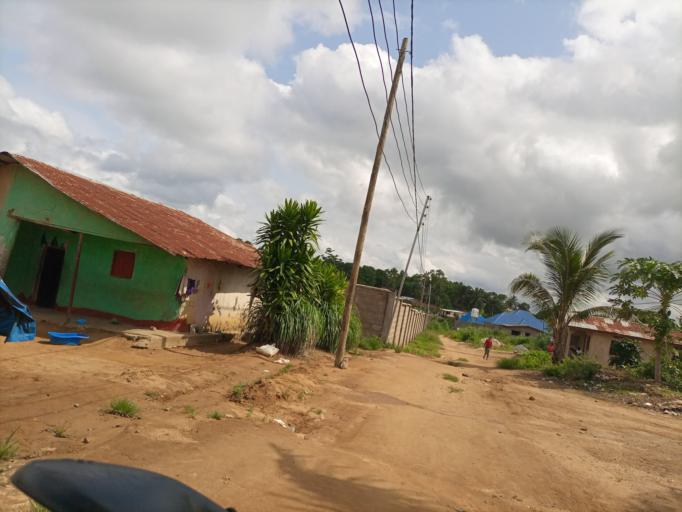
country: SL
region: Southern Province
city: Bo
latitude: 7.9621
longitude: -11.7612
